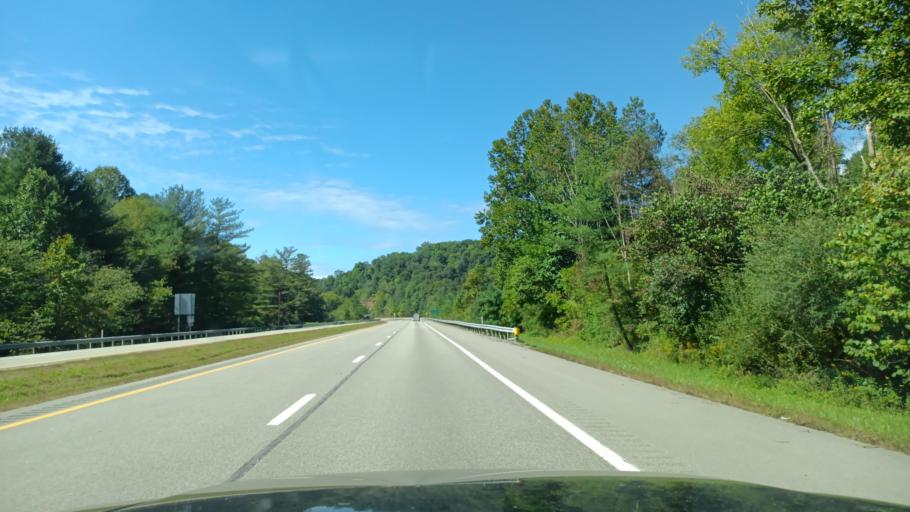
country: US
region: West Virginia
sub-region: Harrison County
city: Salem
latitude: 39.2977
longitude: -80.5751
